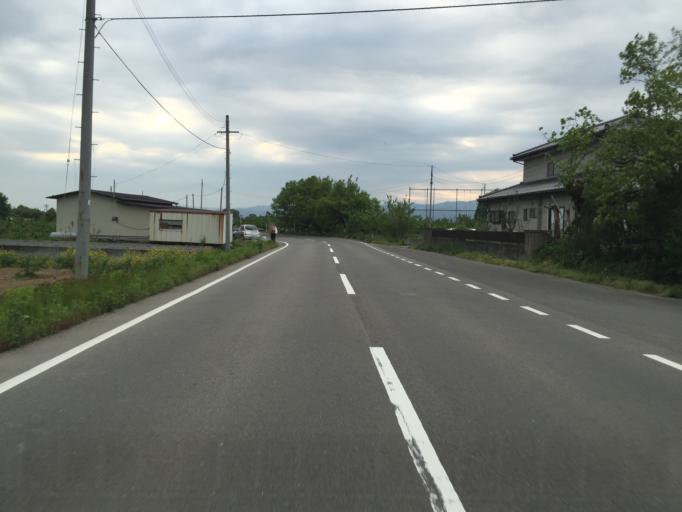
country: JP
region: Fukushima
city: Hobaramachi
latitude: 37.8281
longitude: 140.5370
